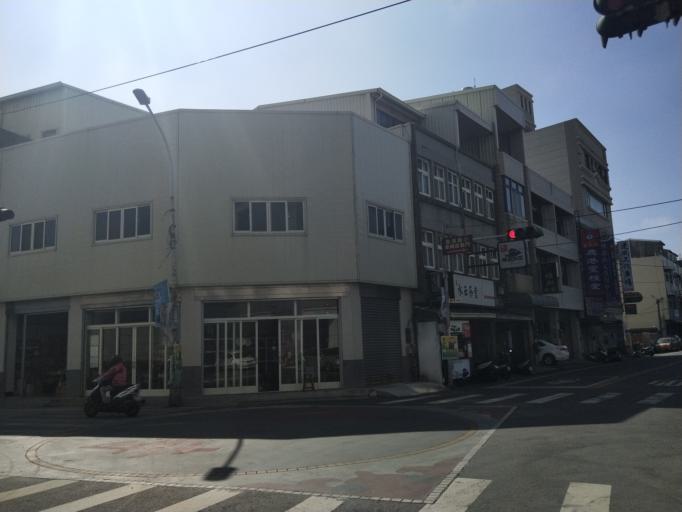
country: TW
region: Taiwan
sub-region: Changhua
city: Chang-hua
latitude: 24.0508
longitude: 120.4347
